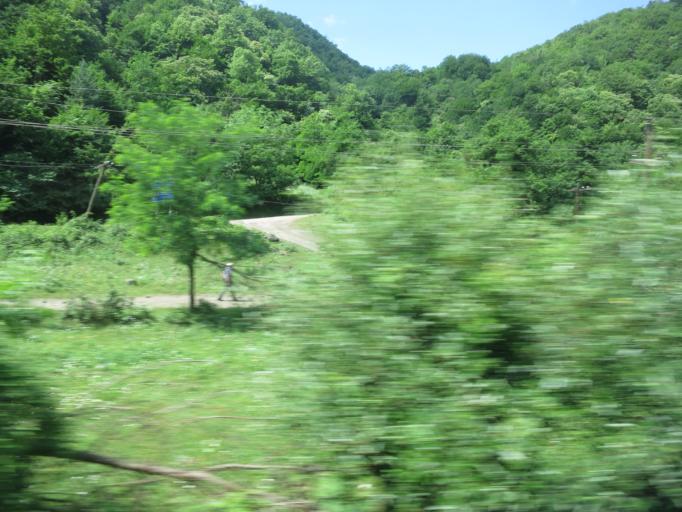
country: GE
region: Imereti
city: Kharagauli
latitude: 42.0008
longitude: 43.2243
